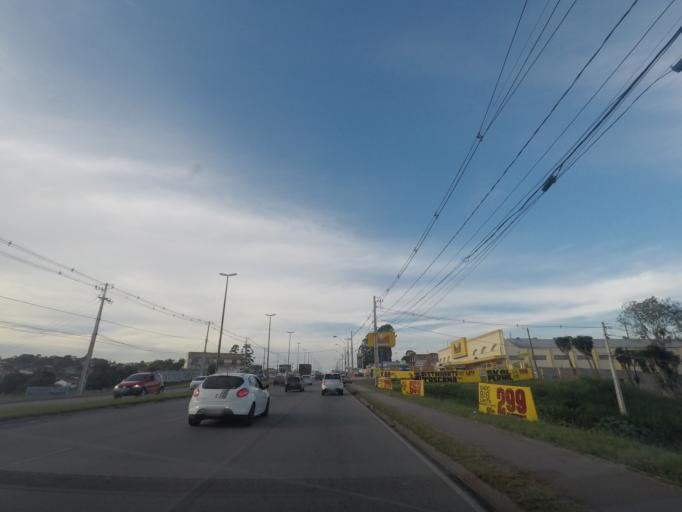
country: BR
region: Parana
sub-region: Pinhais
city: Pinhais
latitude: -25.3723
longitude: -49.1916
